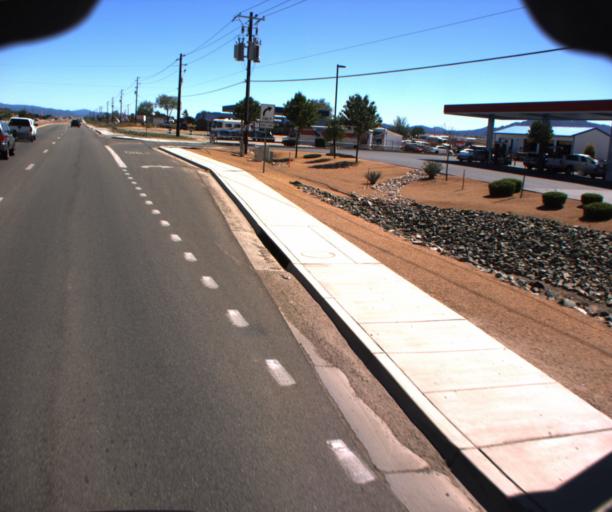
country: US
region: Arizona
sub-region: Yavapai County
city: Chino Valley
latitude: 34.7308
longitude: -112.4542
